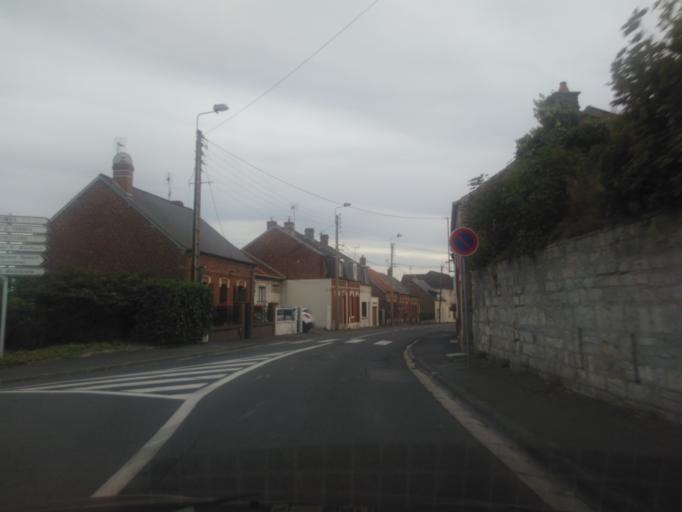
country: FR
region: Picardie
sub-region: Departement de l'Aisne
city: Laon
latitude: 49.5651
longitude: 3.6355
